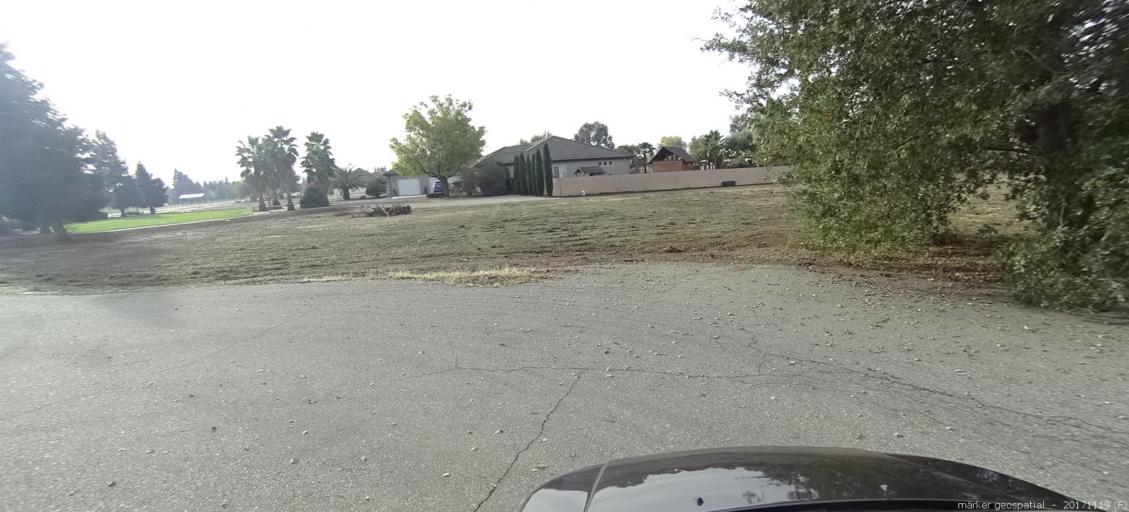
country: US
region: California
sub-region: Shasta County
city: Anderson
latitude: 40.5117
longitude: -122.3301
